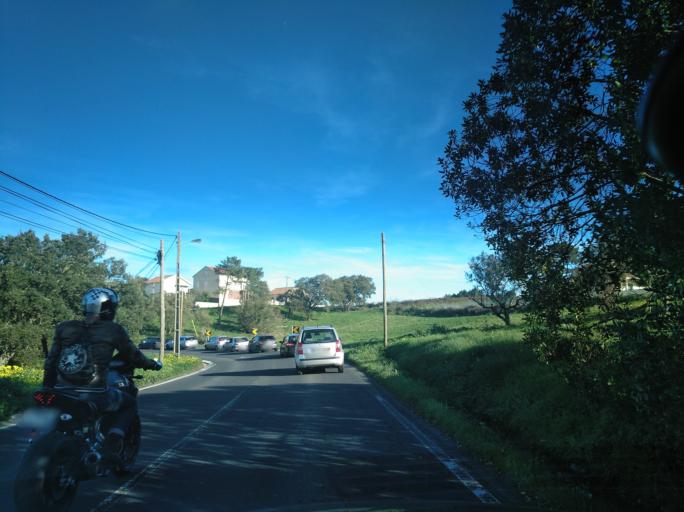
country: PT
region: Lisbon
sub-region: Mafra
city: Mafra
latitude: 38.9260
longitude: -9.3144
